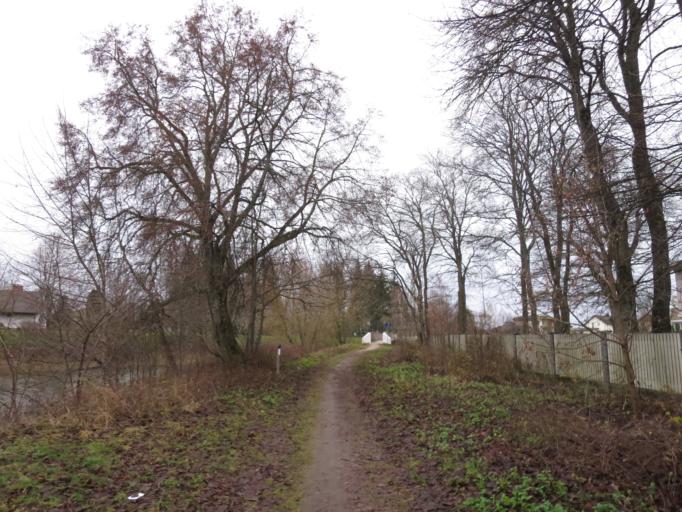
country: LV
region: Adazi
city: Adazi
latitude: 57.0741
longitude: 24.3444
